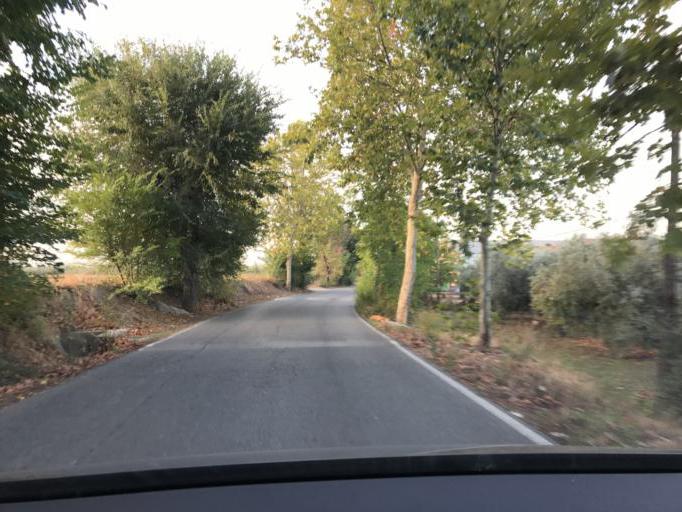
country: ES
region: Andalusia
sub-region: Provincia de Granada
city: Jun
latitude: 37.2224
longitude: -3.5997
